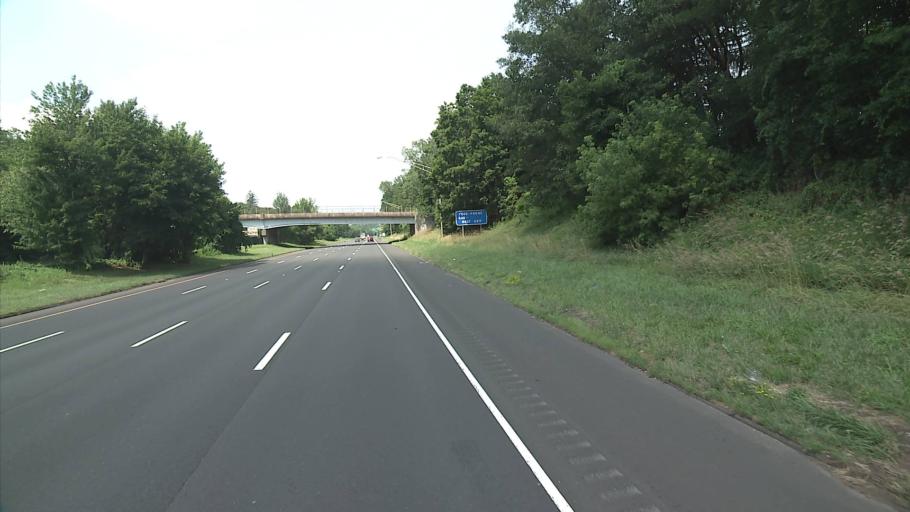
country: US
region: Connecticut
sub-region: Hartford County
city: Manchester
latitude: 41.7630
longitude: -72.5295
